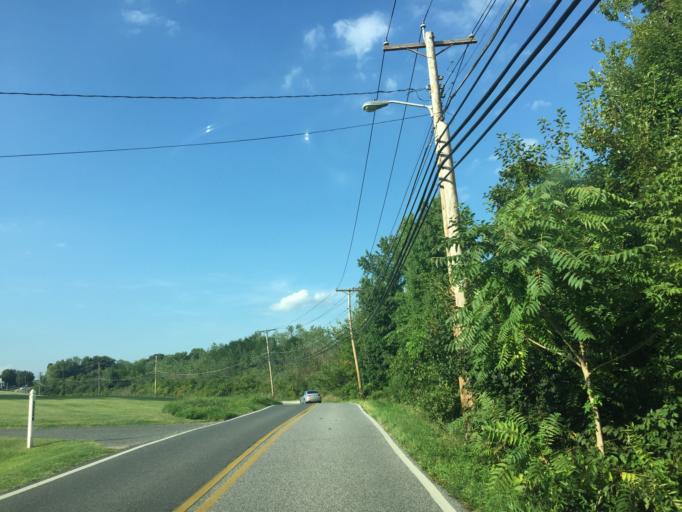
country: US
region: Maryland
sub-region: Baltimore County
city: Rosedale
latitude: 39.3320
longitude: -76.5221
